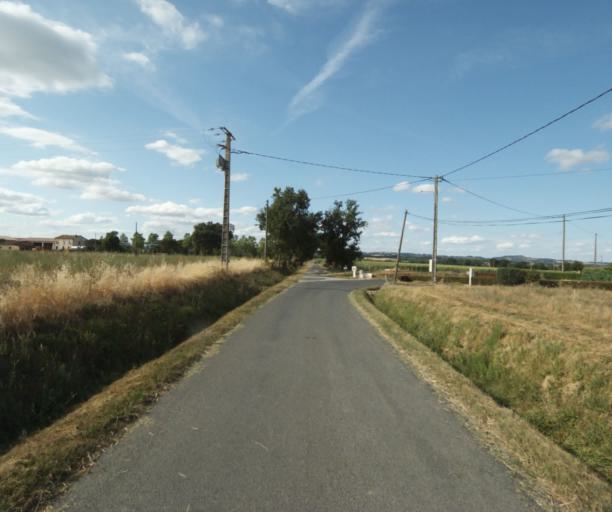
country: FR
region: Midi-Pyrenees
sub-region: Departement de la Haute-Garonne
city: Revel
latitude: 43.5068
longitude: 1.9971
